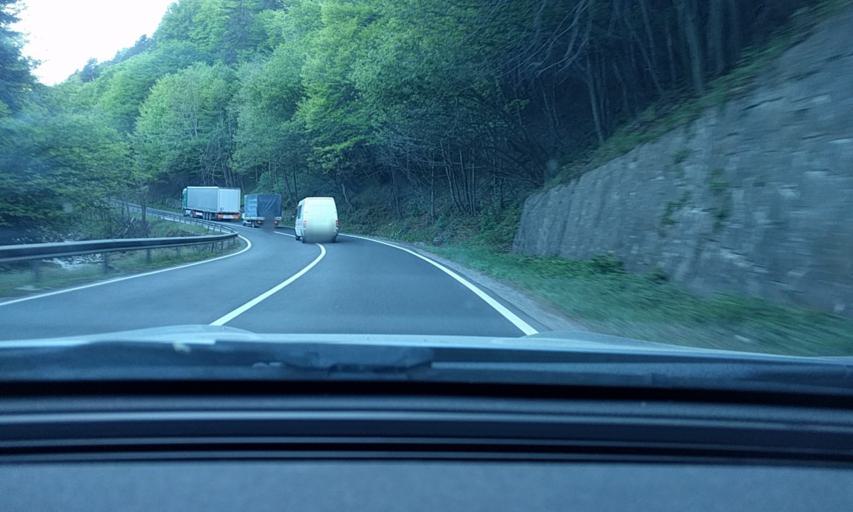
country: RO
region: Covasna
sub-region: Comuna Bretcu
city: Bretcu
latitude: 46.0932
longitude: 26.4057
